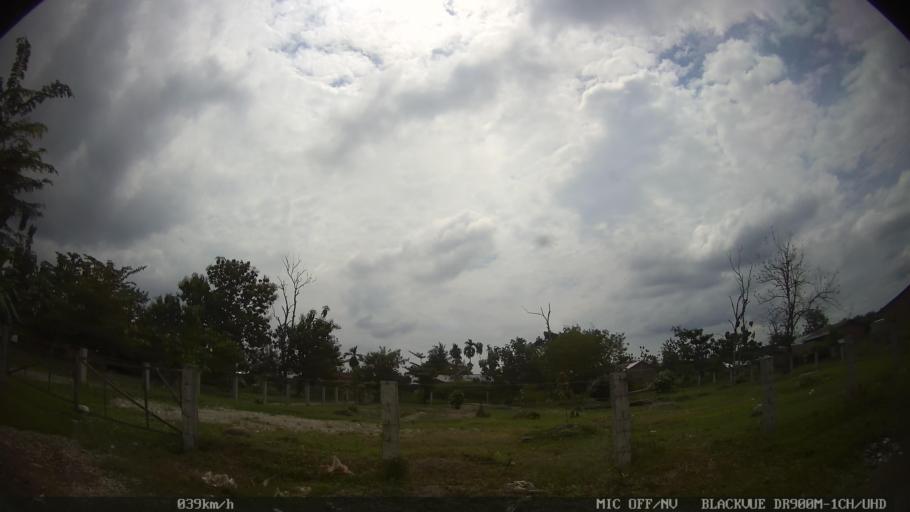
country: ID
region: North Sumatra
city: Sunggal
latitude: 3.6351
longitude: 98.6061
